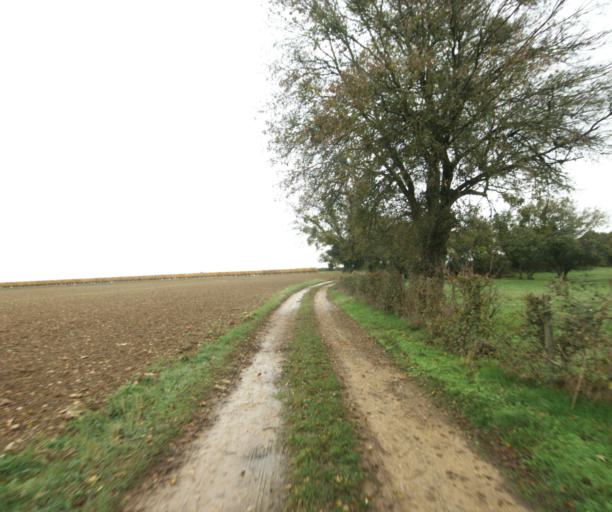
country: FR
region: Bourgogne
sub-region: Departement de Saone-et-Loire
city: Tournus
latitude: 46.4874
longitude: 4.8607
